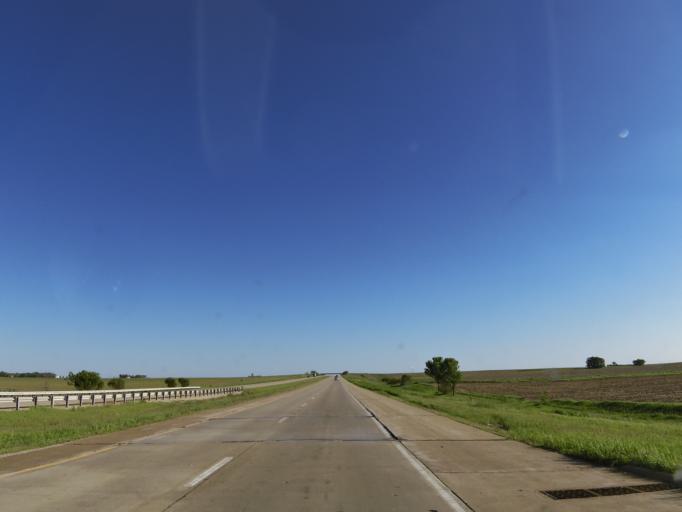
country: US
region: Illinois
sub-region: Woodford County
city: El Paso
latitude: 40.8003
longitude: -89.0359
